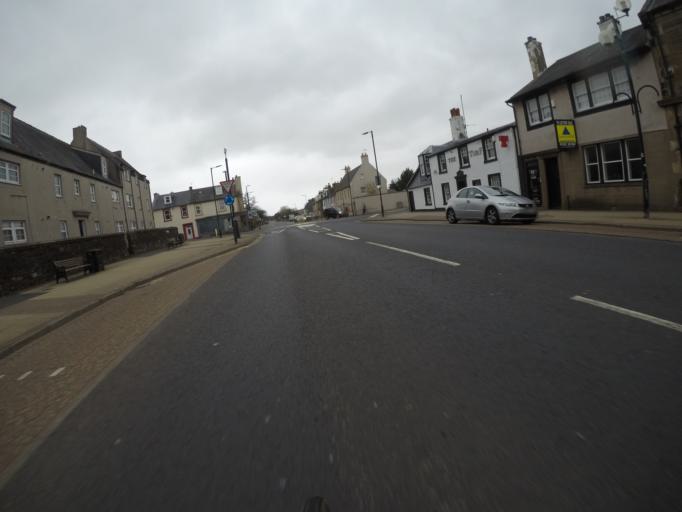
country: GB
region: Scotland
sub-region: North Ayrshire
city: Irvine
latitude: 55.6175
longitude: -4.6690
